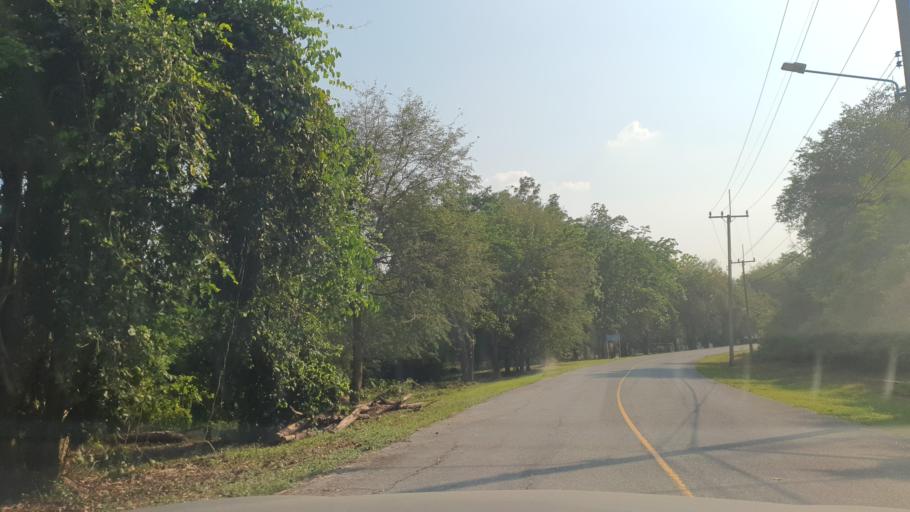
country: TH
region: Kanchanaburi
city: Sai Yok
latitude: 14.2261
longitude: 99.2305
